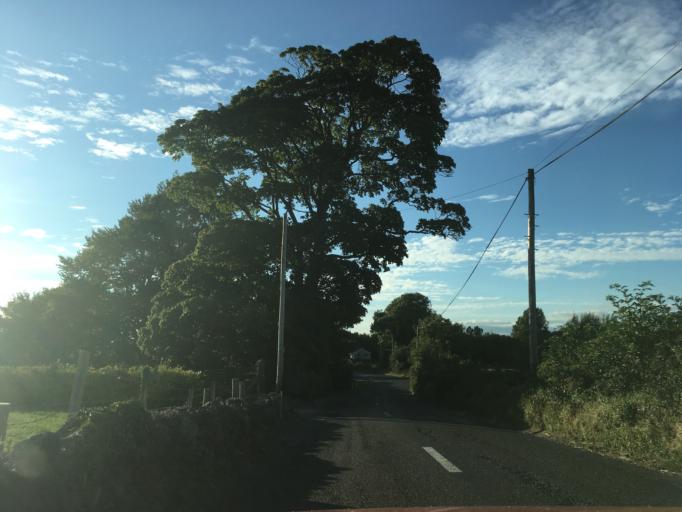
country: IE
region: Munster
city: Cashel
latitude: 52.4536
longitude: -7.9126
